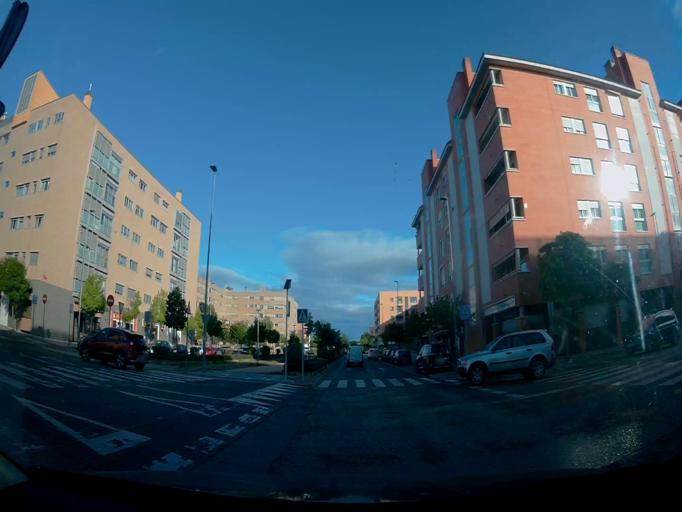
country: ES
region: Madrid
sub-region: Provincia de Madrid
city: San Sebastian de los Reyes
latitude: 40.5612
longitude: -3.6136
